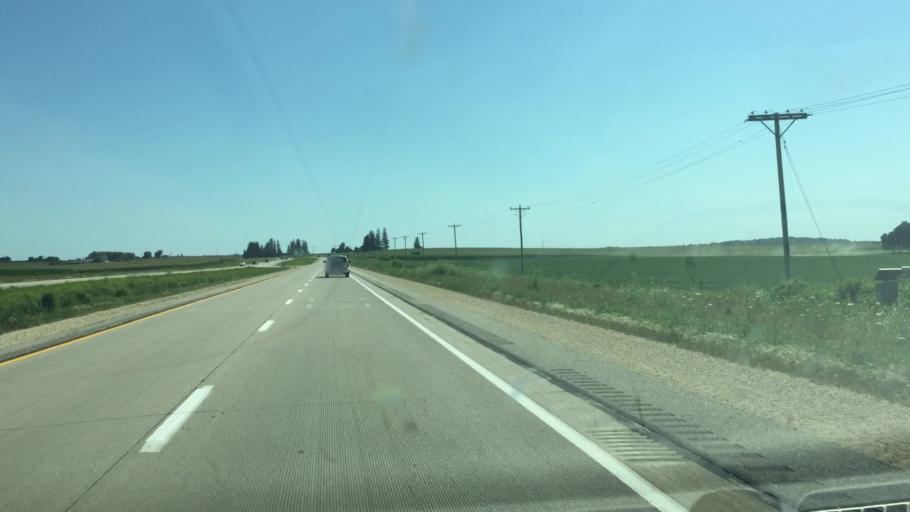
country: US
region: Iowa
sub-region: Jones County
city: Monticello
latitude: 42.1822
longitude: -91.2232
